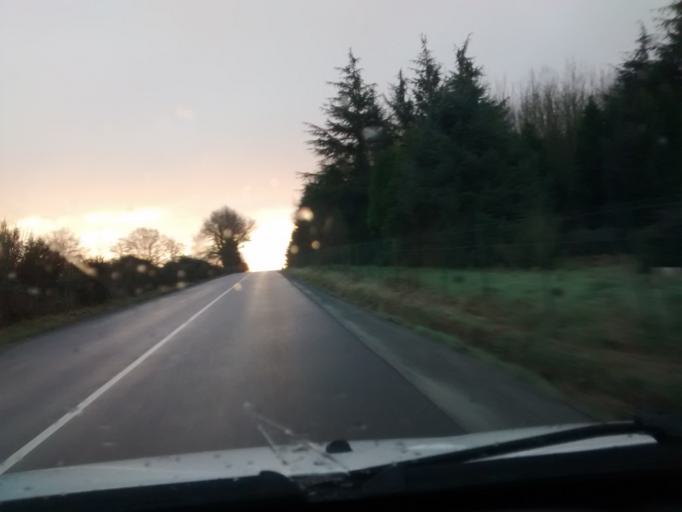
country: FR
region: Brittany
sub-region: Departement d'Ille-et-Vilaine
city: Louvigne-de-Bais
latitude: 48.0269
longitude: -1.3133
